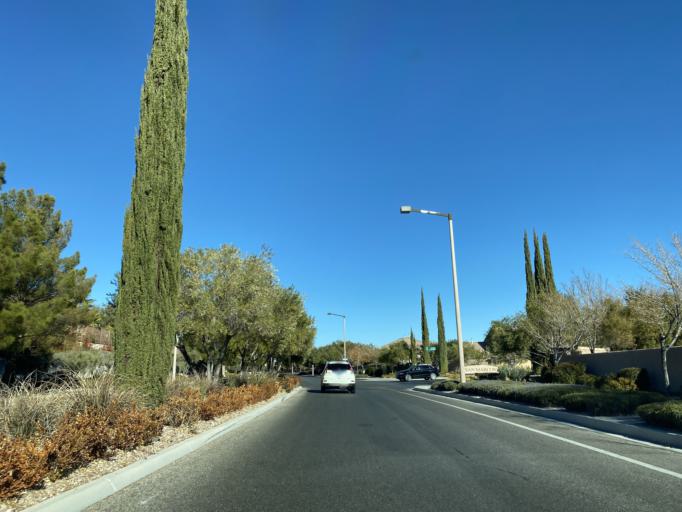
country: US
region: Nevada
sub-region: Clark County
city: Summerlin South
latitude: 36.1713
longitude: -115.3423
